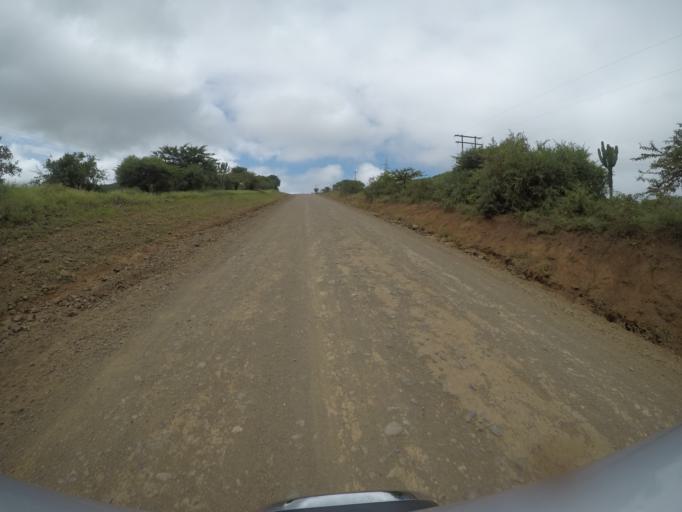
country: ZA
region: KwaZulu-Natal
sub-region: uThungulu District Municipality
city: Empangeni
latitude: -28.6310
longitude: 31.8723
